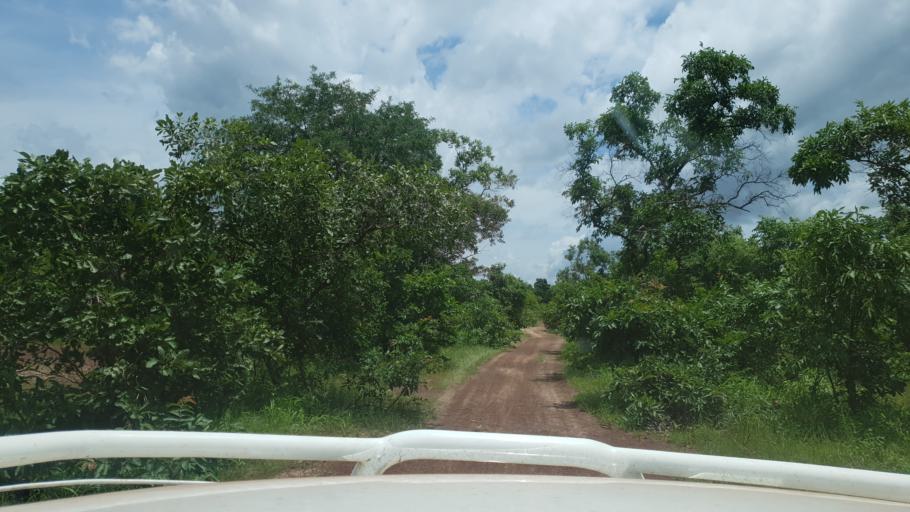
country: ML
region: Koulikoro
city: Banamba
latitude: 13.1947
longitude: -7.3214
